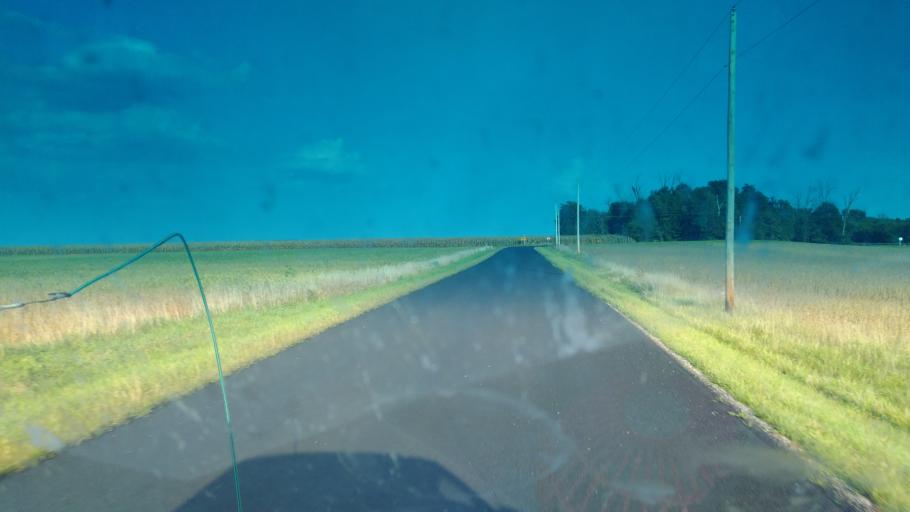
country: US
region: Ohio
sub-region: Crawford County
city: Bucyrus
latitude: 40.9660
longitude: -82.9994
